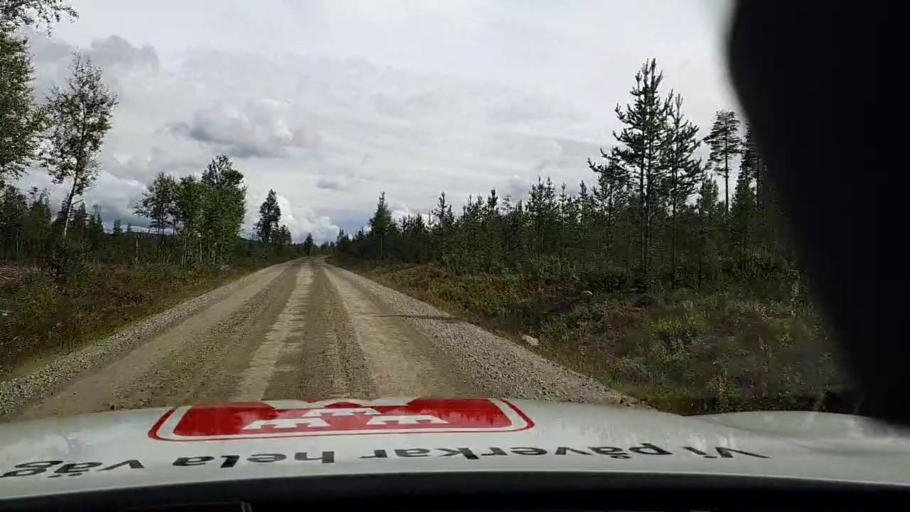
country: SE
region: Jaemtland
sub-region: Are Kommun
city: Jarpen
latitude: 62.5086
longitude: 13.4944
